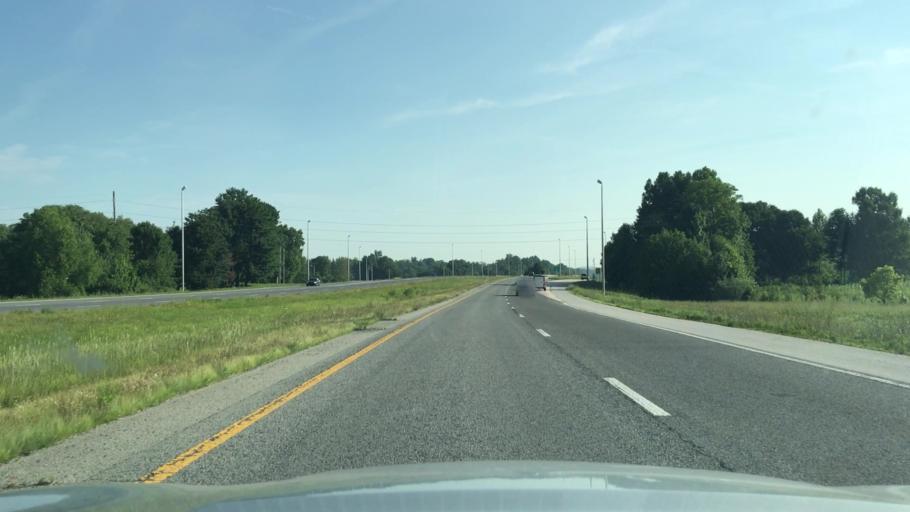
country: US
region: Tennessee
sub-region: Putnam County
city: Cookeville
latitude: 36.1478
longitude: -85.4762
